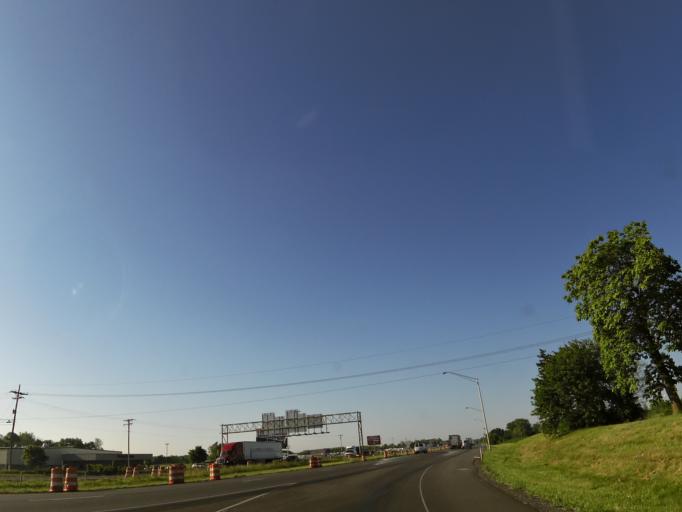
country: US
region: Indiana
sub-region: Jackson County
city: Seymour
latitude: 38.9554
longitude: -85.8437
